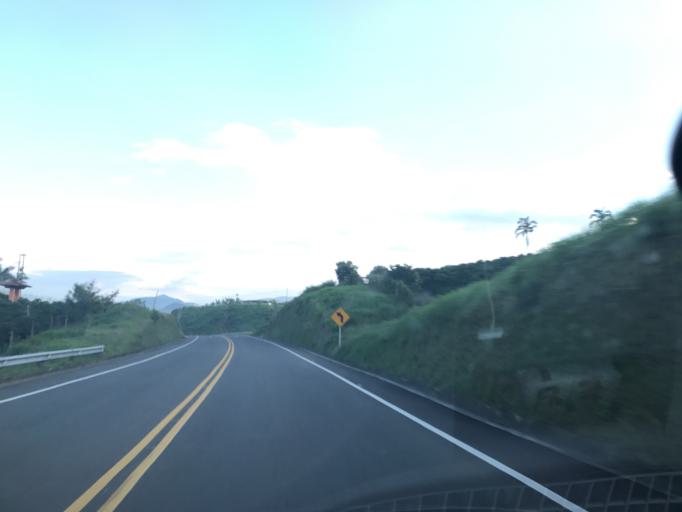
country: CO
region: Risaralda
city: Pereira
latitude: 4.7676
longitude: -75.7078
